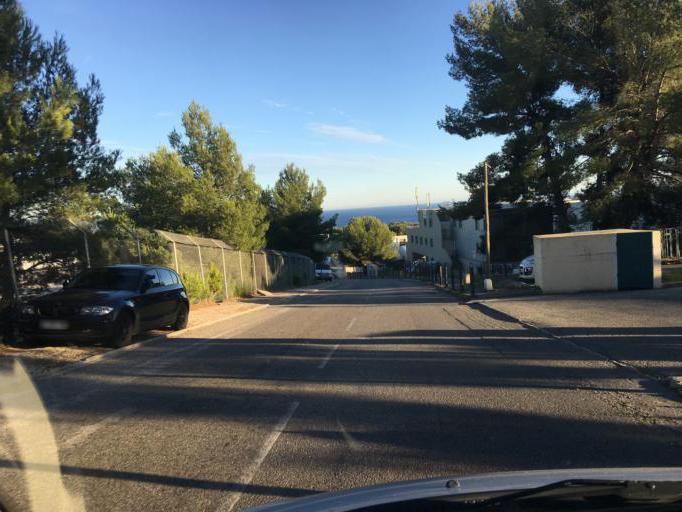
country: FR
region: Provence-Alpes-Cote d'Azur
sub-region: Departement des Bouches-du-Rhone
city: Ceyreste
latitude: 43.2084
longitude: 5.5994
